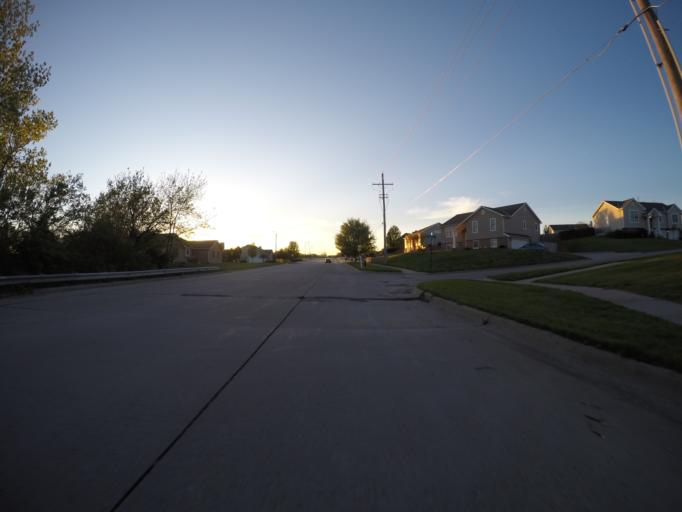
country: US
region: Kansas
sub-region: Riley County
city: Manhattan
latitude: 39.1655
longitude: -96.6142
